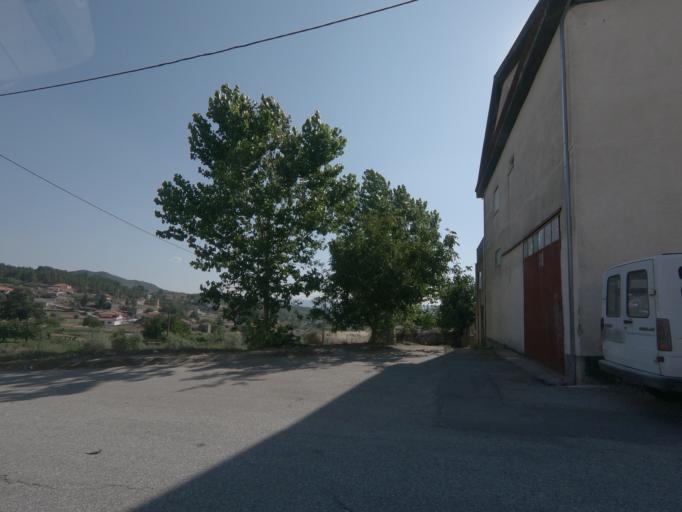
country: PT
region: Viseu
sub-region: Tabuaco
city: Tabuaco
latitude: 41.0508
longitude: -7.5674
